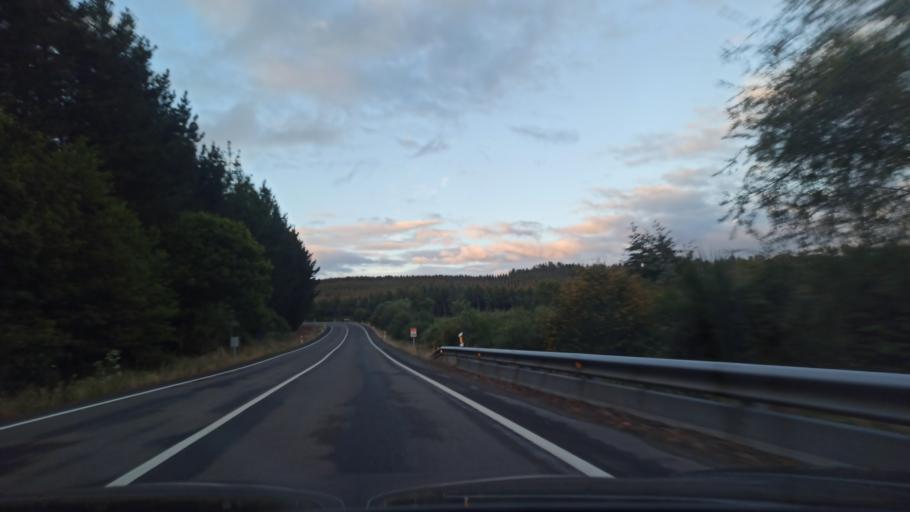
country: ES
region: Galicia
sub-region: Provincia de Lugo
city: Monterroso
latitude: 42.8015
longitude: -7.7896
